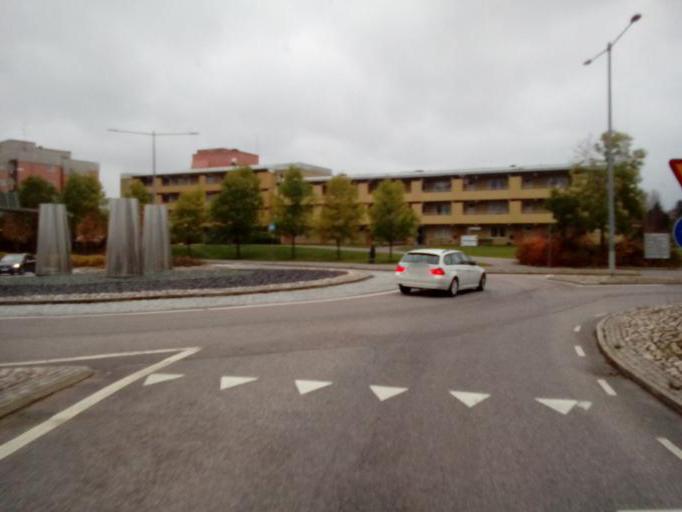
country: SE
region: OErebro
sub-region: Degerfors Kommun
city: Degerfors
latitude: 59.2357
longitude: 14.4300
